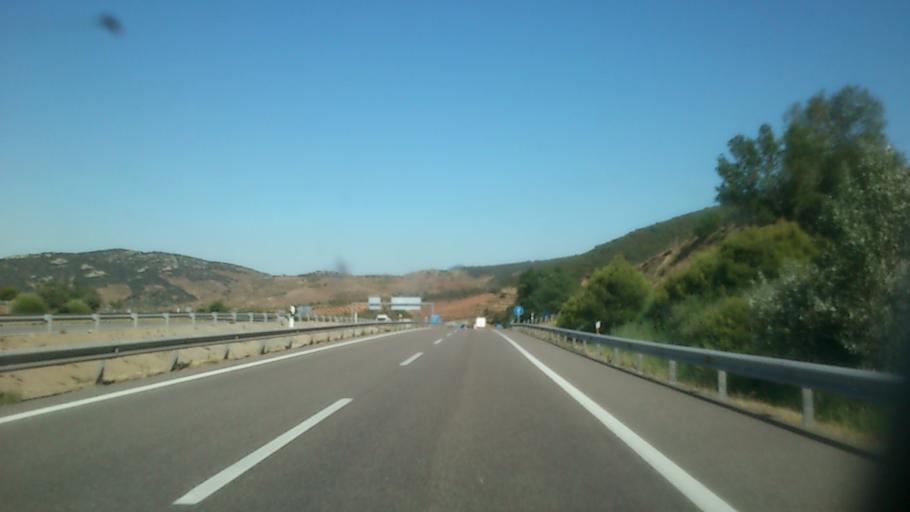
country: ES
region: Aragon
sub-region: Provincia de Zaragoza
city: Paracuellos de la Ribera
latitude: 41.4131
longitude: -1.5172
